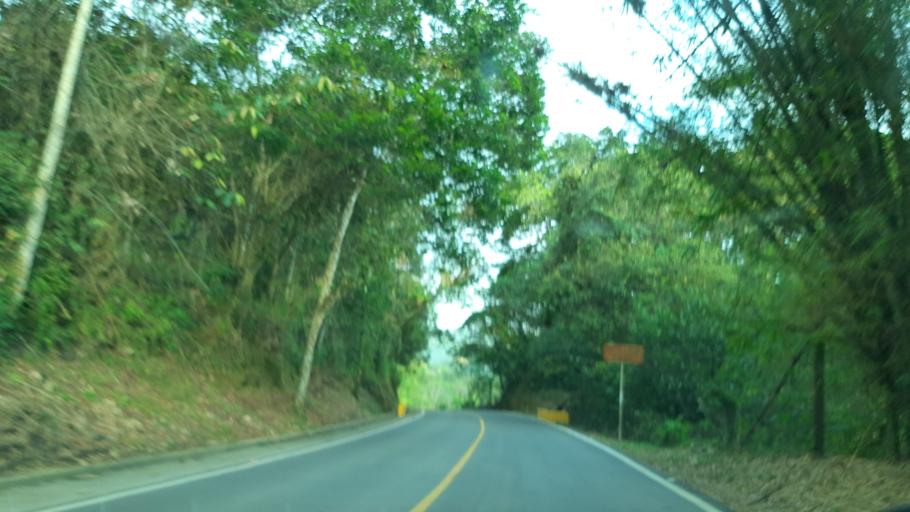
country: CO
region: Boyaca
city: San Luis de Gaceno
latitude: 4.8178
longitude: -73.1890
